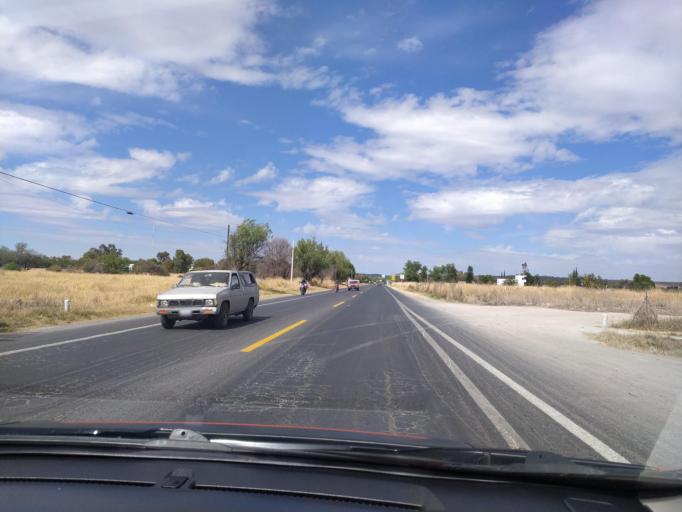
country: LA
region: Oudomxai
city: Muang La
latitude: 21.0173
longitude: 101.8272
